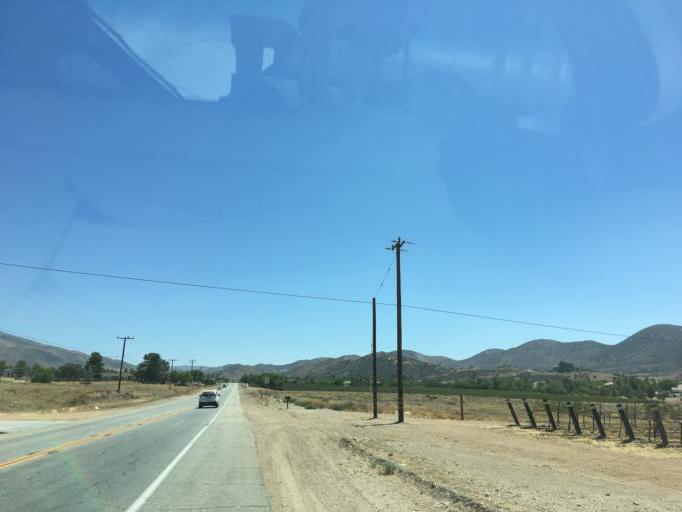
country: US
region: California
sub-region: Los Angeles County
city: Agua Dulce
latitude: 34.5201
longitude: -118.3112
